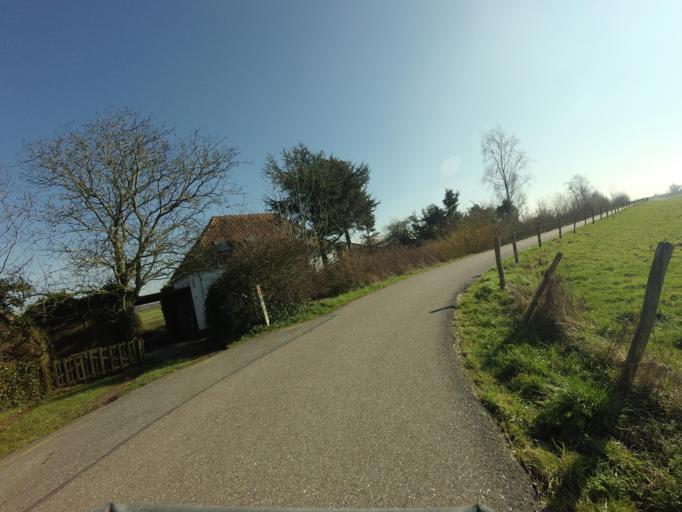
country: NL
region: South Holland
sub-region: Bodegraven-Reeuwijk
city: Bodegraven
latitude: 52.0803
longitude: 4.7857
